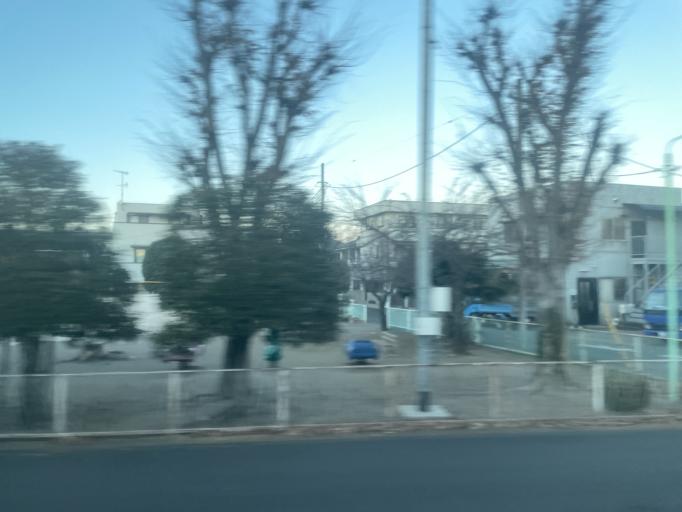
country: JP
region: Saitama
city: Fukayacho
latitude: 36.1892
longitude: 139.2906
